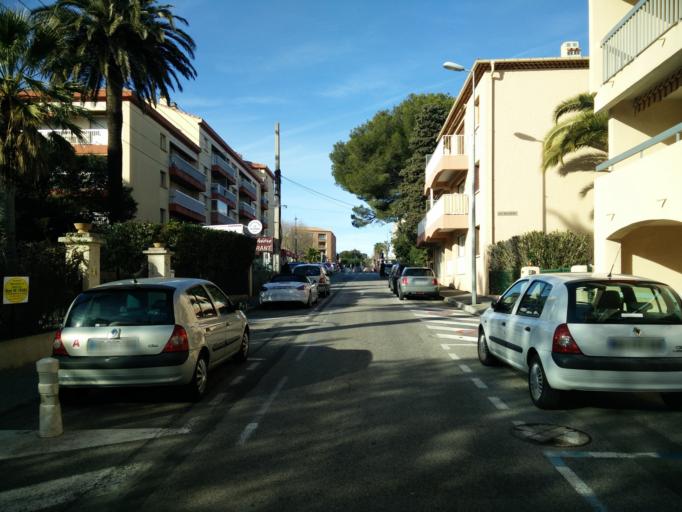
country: FR
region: Provence-Alpes-Cote d'Azur
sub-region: Departement du Var
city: Frejus
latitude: 43.3857
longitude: 6.7243
